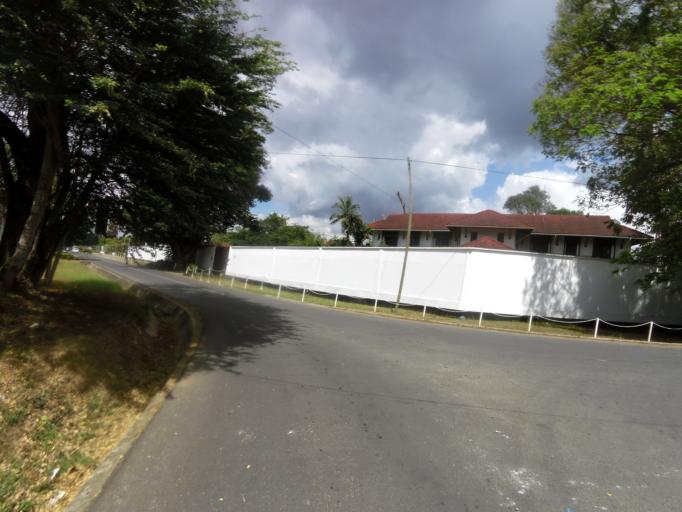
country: TZ
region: Dar es Salaam
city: Magomeni
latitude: -6.7883
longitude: 39.2802
